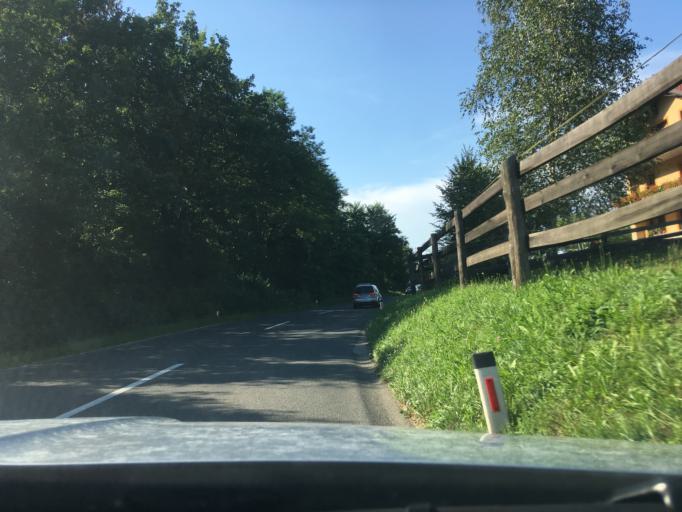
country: SI
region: Crnomelj
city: Crnomelj
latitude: 45.5083
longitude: 15.1867
